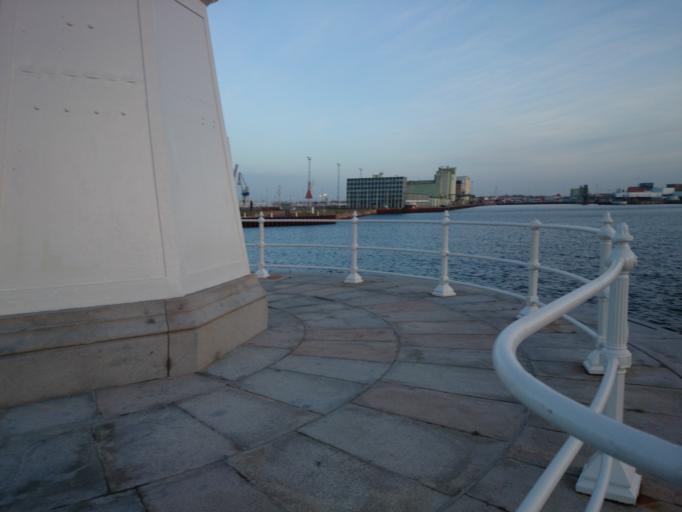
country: SE
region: Skane
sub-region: Malmo
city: Malmoe
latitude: 55.6164
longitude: 12.9916
